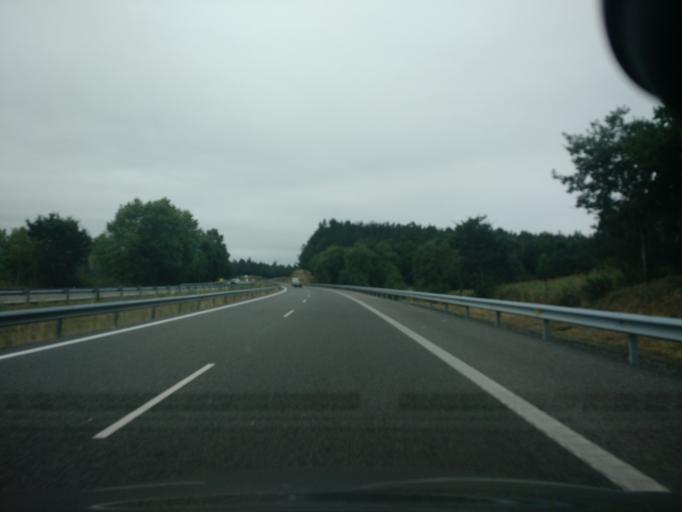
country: ES
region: Galicia
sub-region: Provincia da Coruna
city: Oroso
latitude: 43.0099
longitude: -8.4195
